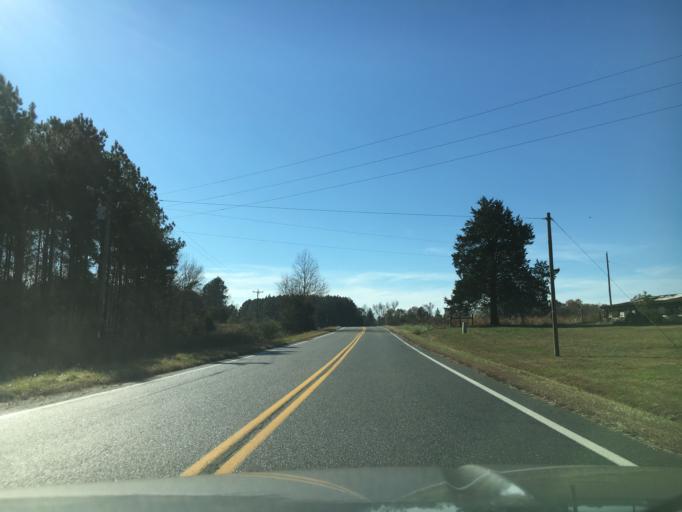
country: US
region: Virginia
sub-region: Cumberland County
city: Cumberland
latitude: 37.5457
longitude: -78.1909
